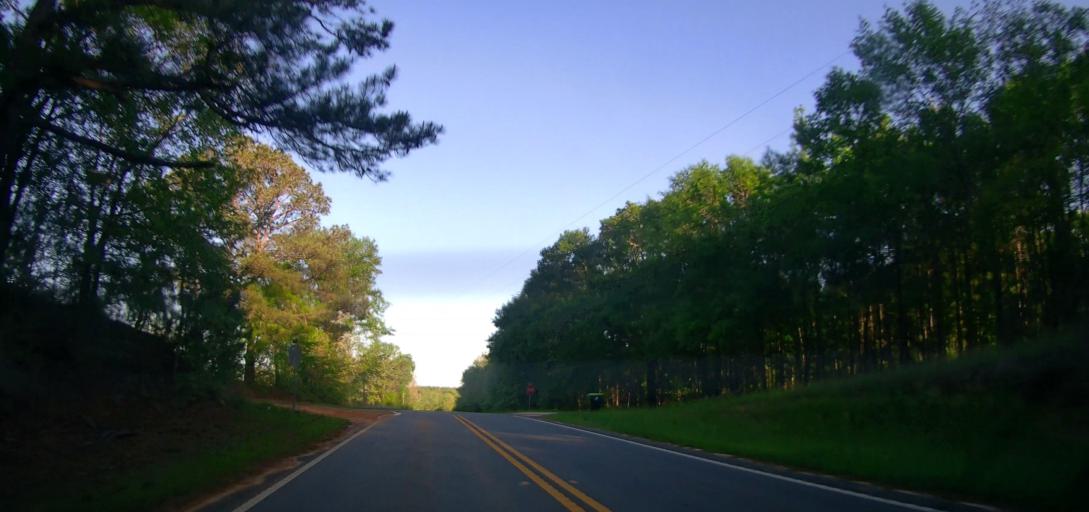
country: US
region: Georgia
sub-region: Marion County
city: Buena Vista
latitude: 32.3571
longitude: -84.3885
